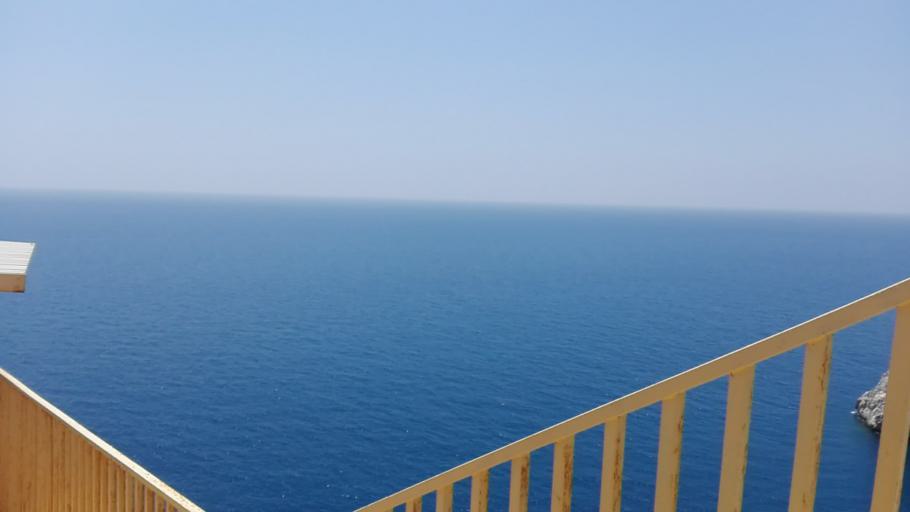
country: TR
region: Mersin
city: Aydincik
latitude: 36.1310
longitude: 33.4027
